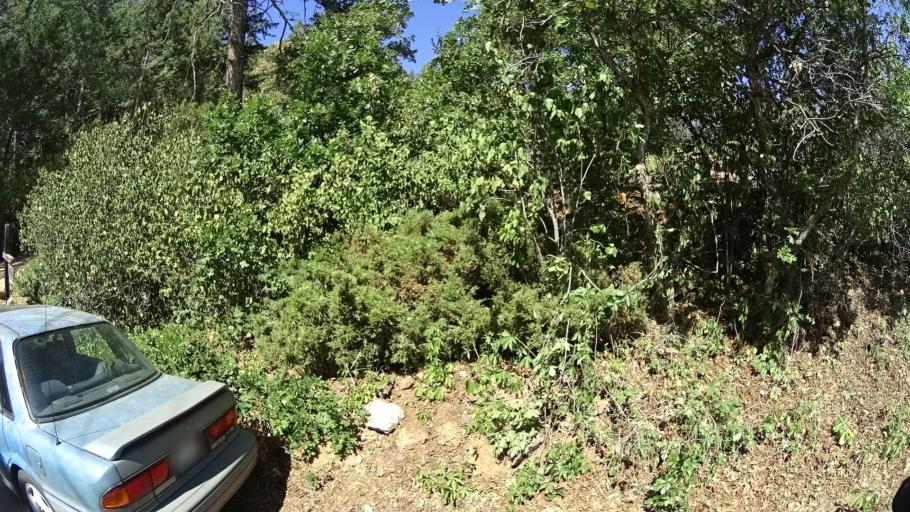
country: US
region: Colorado
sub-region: El Paso County
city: Colorado Springs
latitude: 38.8084
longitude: -104.8794
